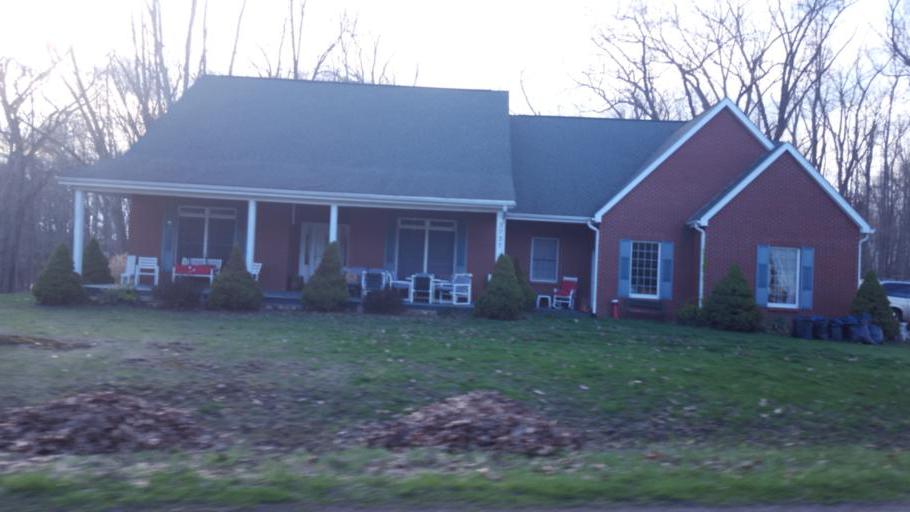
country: US
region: Ohio
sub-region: Knox County
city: Gambier
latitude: 40.4279
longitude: -82.3401
